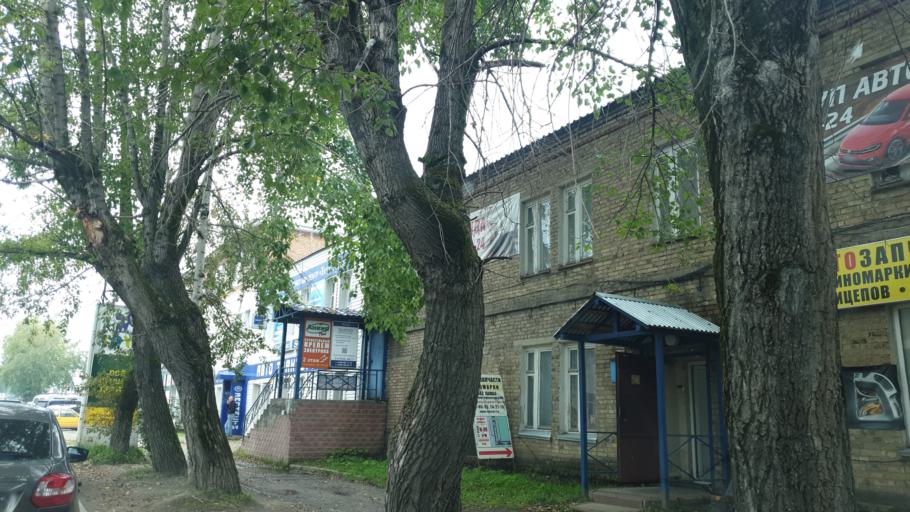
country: RU
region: Komi Republic
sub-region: Syktyvdinskiy Rayon
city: Syktyvkar
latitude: 61.6556
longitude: 50.8293
